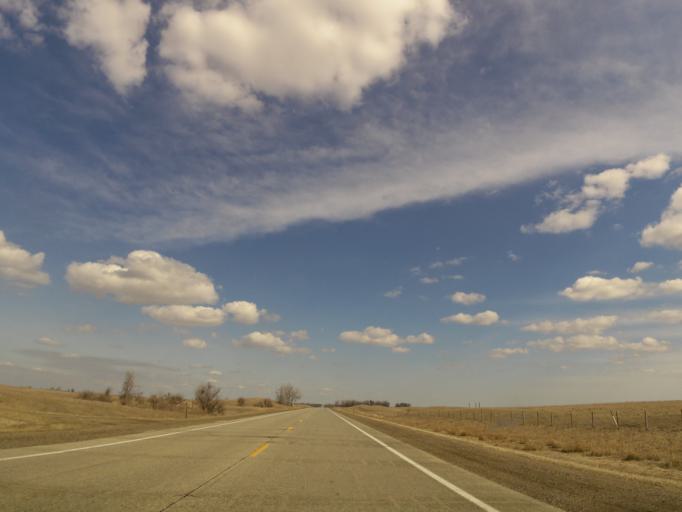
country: US
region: South Dakota
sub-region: Deuel County
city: Clear Lake
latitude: 44.8900
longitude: -96.7204
